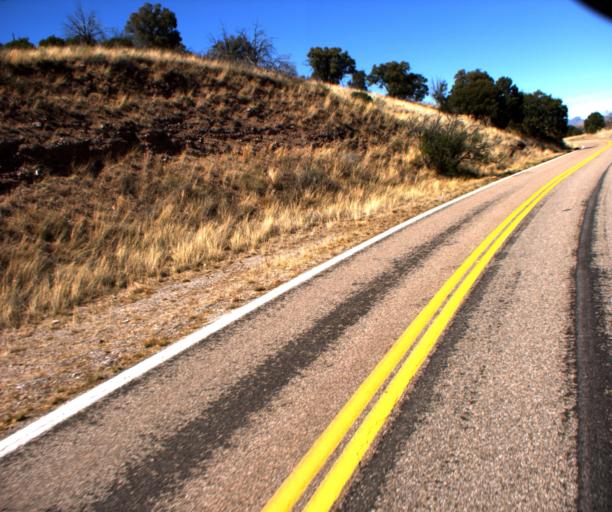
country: US
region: Arizona
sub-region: Cochise County
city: Sierra Vista
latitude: 31.4990
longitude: -110.4944
